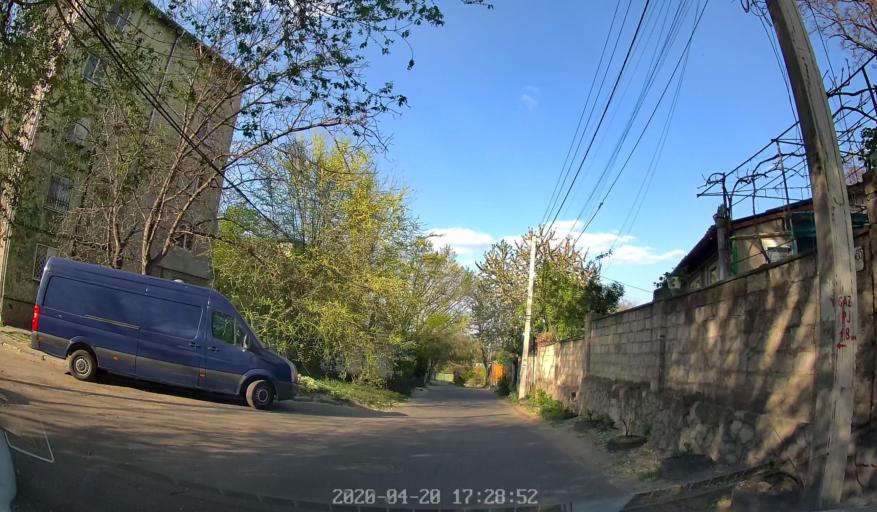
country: MD
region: Chisinau
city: Chisinau
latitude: 46.9961
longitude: 28.8742
